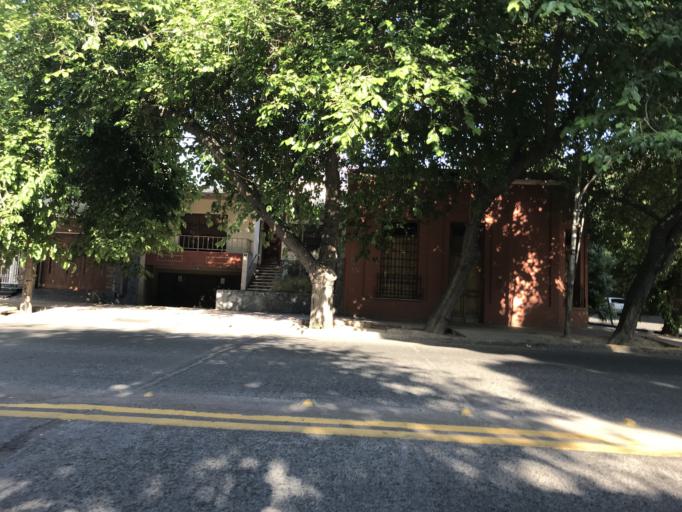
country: AR
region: Mendoza
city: Mendoza
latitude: -32.8809
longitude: -68.8421
